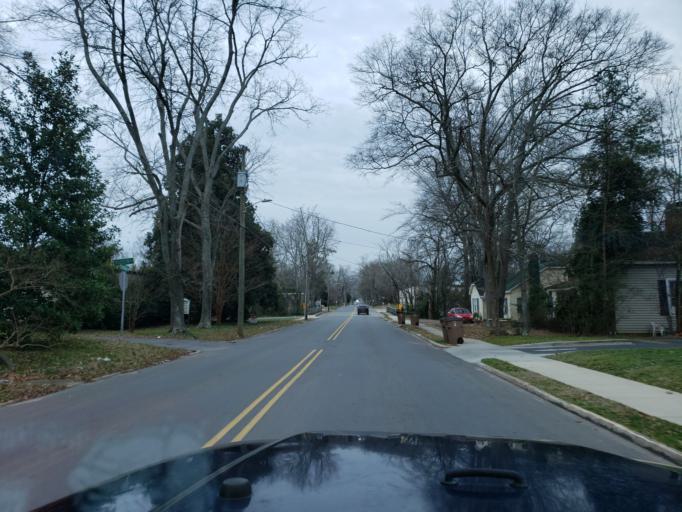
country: US
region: North Carolina
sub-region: Cleveland County
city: Shelby
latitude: 35.2998
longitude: -81.5415
